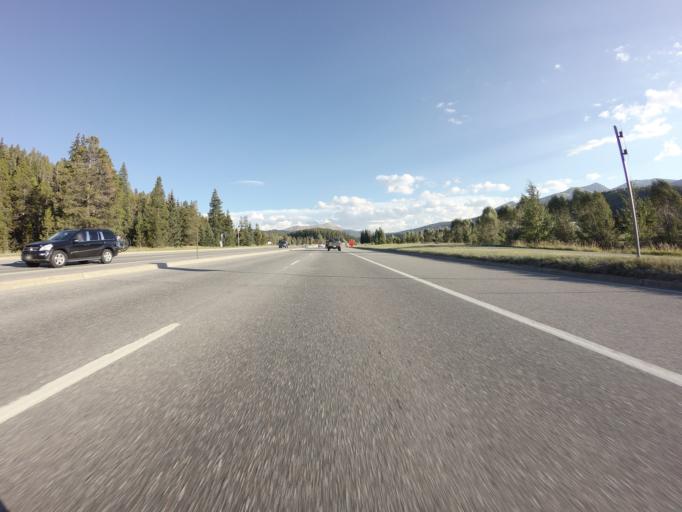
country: US
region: Colorado
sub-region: Summit County
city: Breckenridge
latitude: 39.4975
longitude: -106.0462
